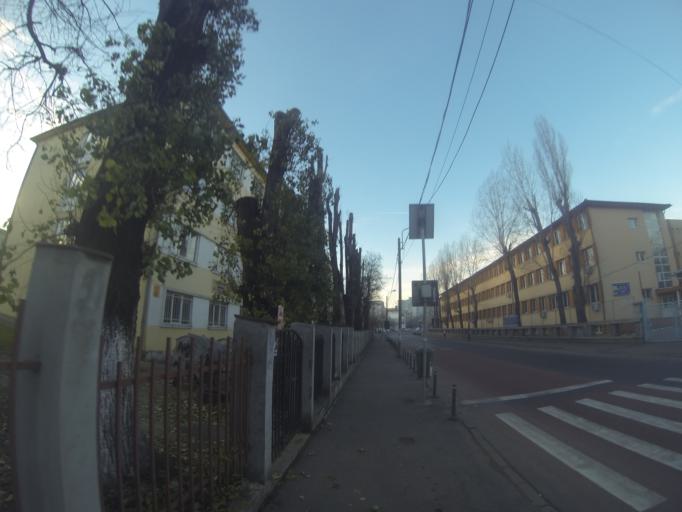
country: RO
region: Bucuresti
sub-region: Municipiul Bucuresti
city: Bucuresti
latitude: 44.4105
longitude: 26.0824
